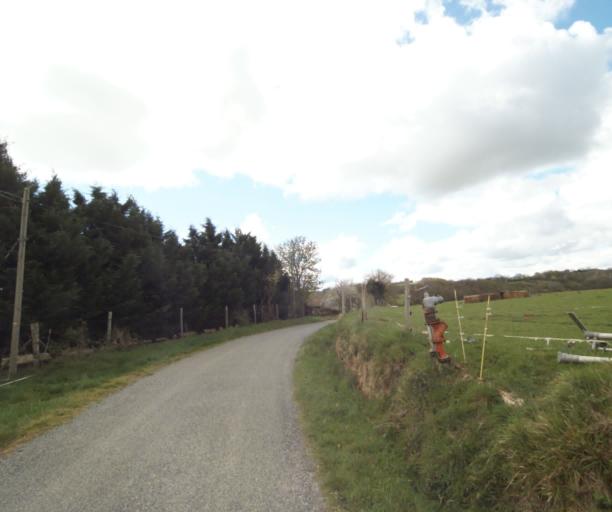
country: FR
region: Midi-Pyrenees
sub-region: Departement de l'Ariege
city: Saverdun
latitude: 43.2063
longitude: 1.5838
